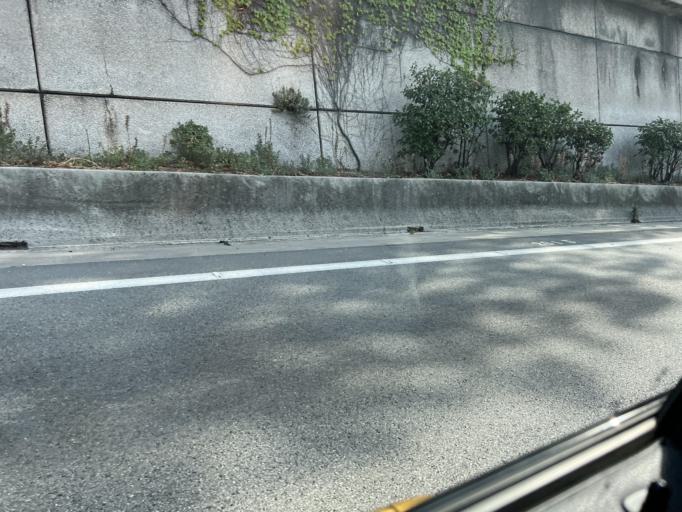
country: FR
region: Provence-Alpes-Cote d'Azur
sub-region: Departement des Alpes-Maritimes
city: La Trinite
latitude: 43.7318
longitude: 7.3007
